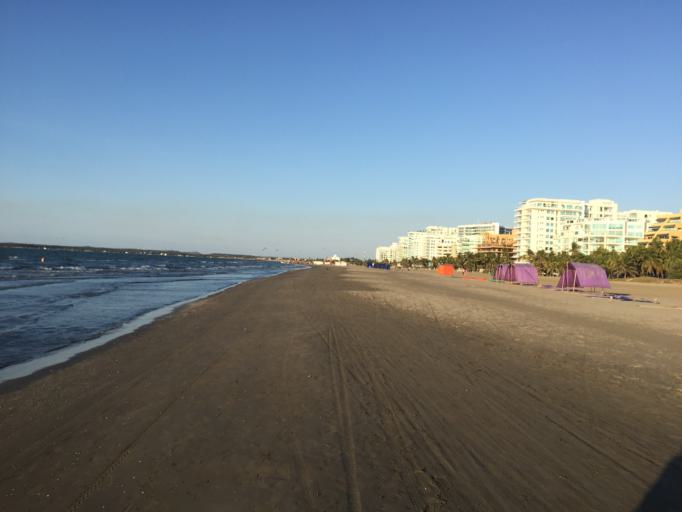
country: CO
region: Bolivar
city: Cartagena
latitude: 10.4621
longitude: -75.5080
